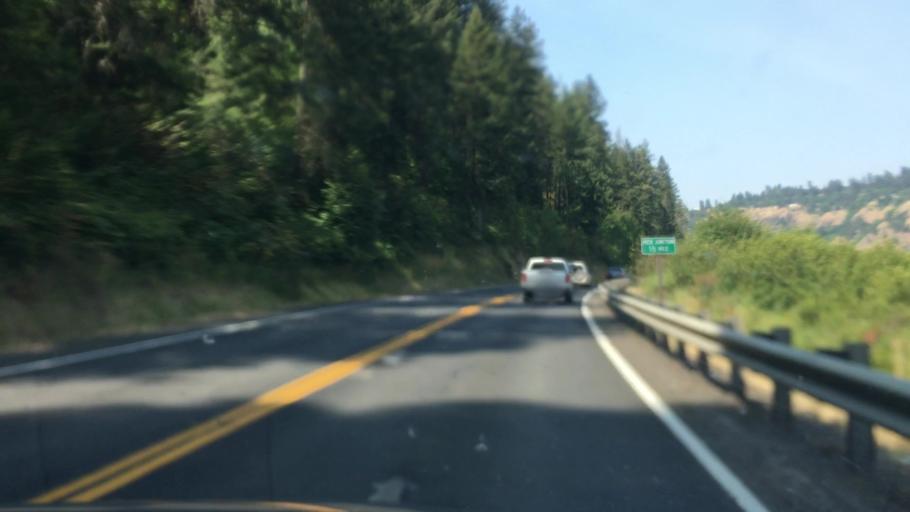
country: US
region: Idaho
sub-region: Clearwater County
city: Orofino
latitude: 46.4969
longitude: -116.4233
